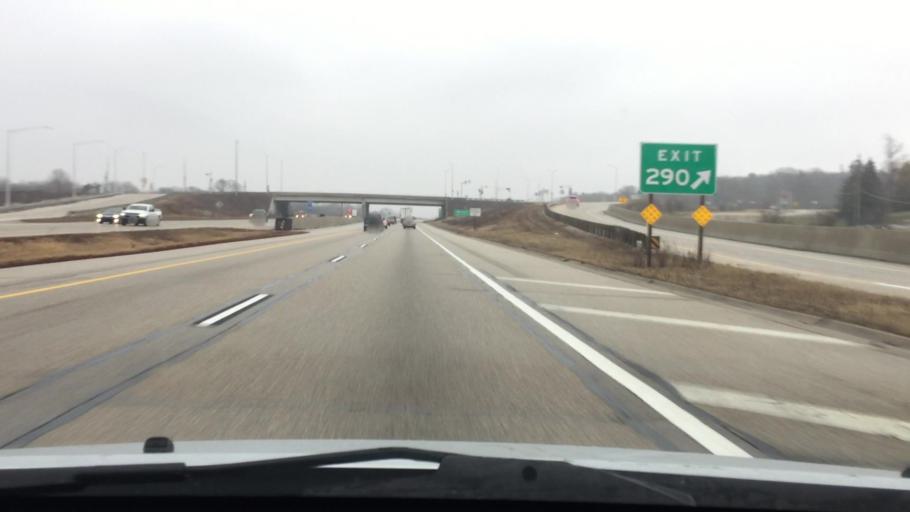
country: US
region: Wisconsin
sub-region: Waukesha County
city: Pewaukee
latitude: 43.0505
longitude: -88.3069
